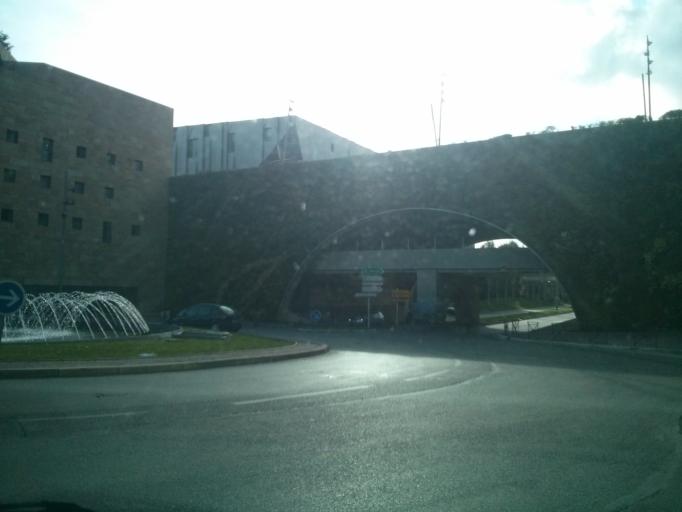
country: FR
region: Provence-Alpes-Cote d'Azur
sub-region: Departement des Bouches-du-Rhone
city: Aix-en-Provence
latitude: 43.5266
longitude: 5.4391
